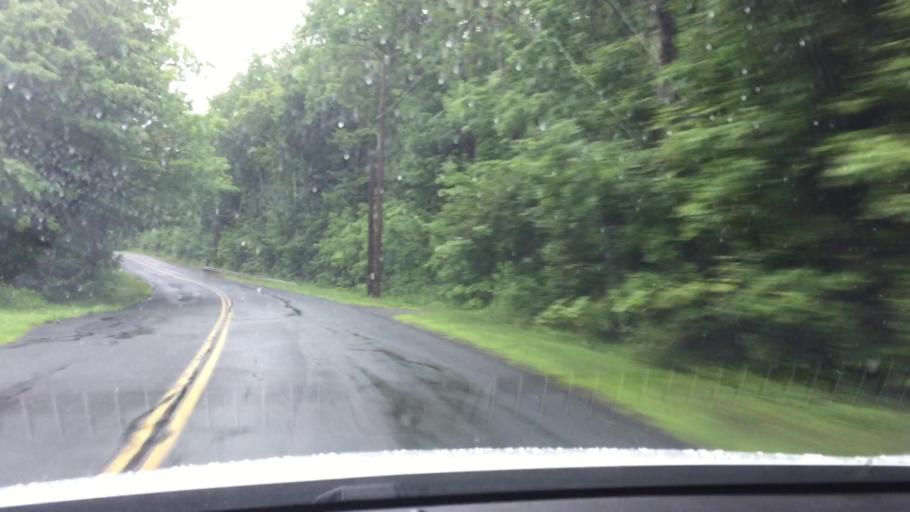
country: US
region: Massachusetts
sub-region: Berkshire County
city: Becket
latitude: 42.3199
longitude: -73.0960
